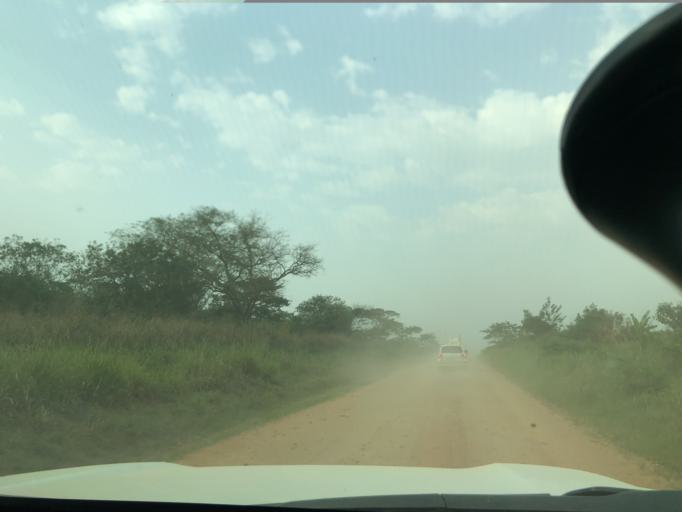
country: UG
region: Western Region
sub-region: Kasese District
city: Margherita
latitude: 0.2115
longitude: 29.6773
